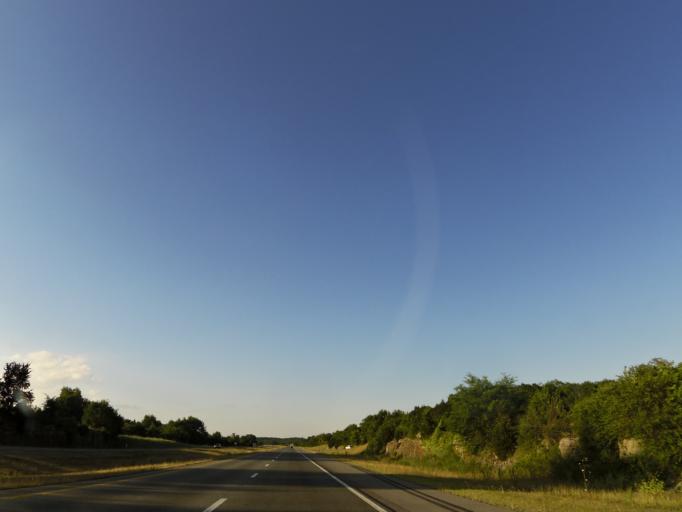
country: US
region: Tennessee
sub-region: Rutherford County
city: Smyrna
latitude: 35.9869
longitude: -86.4375
